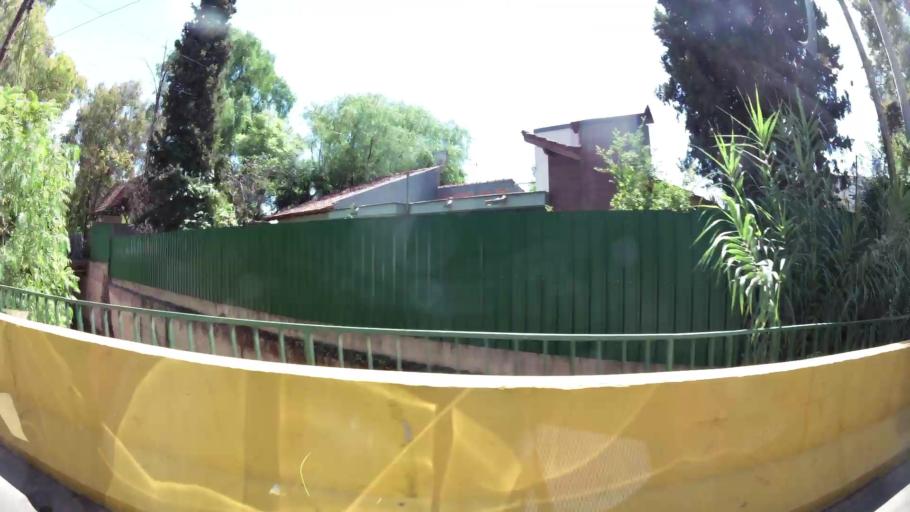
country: AR
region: Mendoza
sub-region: Departamento de Godoy Cruz
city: Godoy Cruz
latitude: -32.9588
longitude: -68.8620
